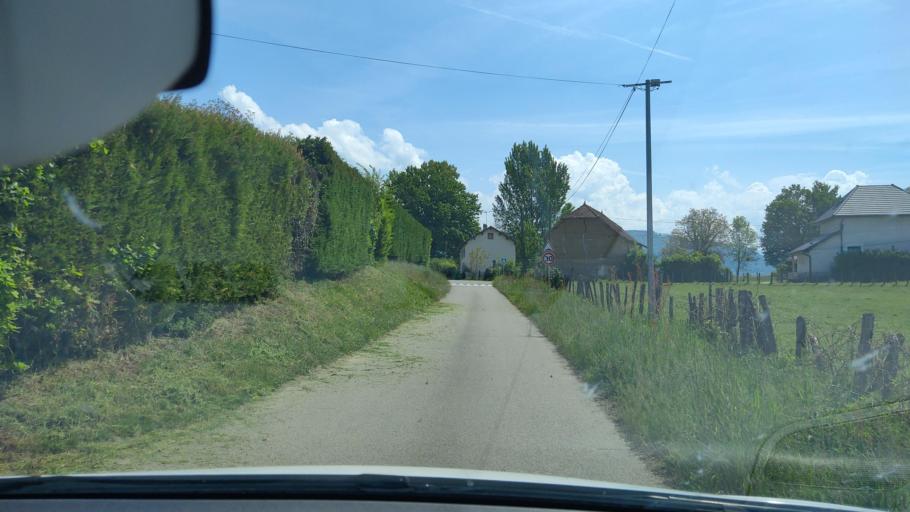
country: FR
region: Rhone-Alpes
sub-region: Departement de la Savoie
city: Domessin
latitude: 45.5278
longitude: 5.7112
